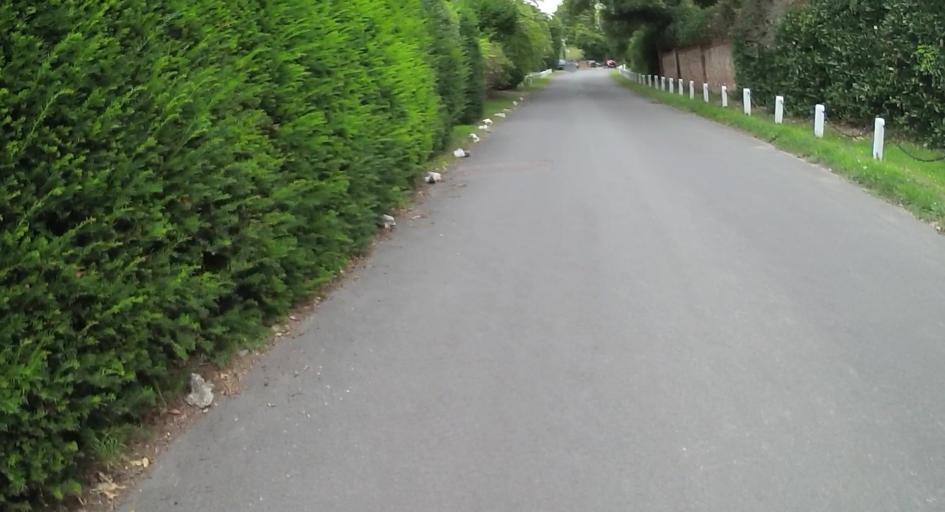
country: GB
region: England
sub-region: Hampshire
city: Kings Worthy
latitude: 51.1550
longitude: -1.3118
